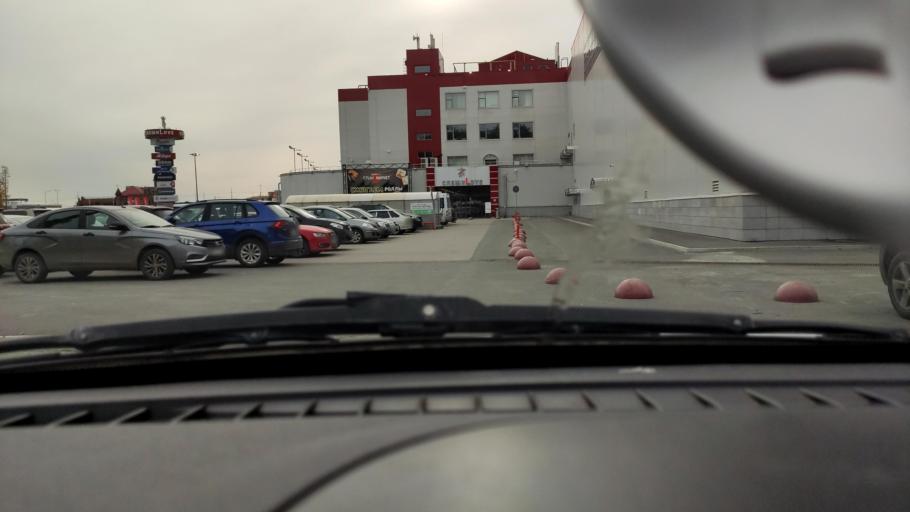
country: RU
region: Perm
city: Perm
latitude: 58.0404
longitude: 56.1935
